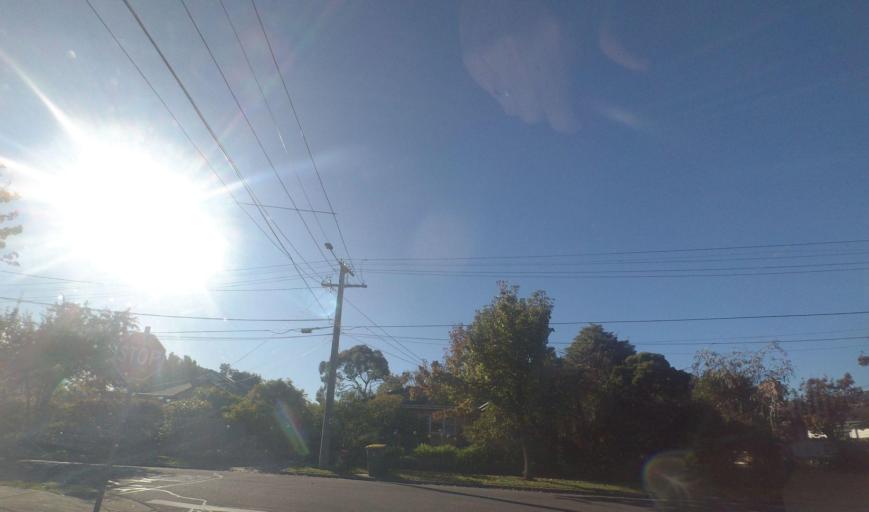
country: AU
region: Victoria
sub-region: Whitehorse
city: Box Hill
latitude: -37.8169
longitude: 145.1367
